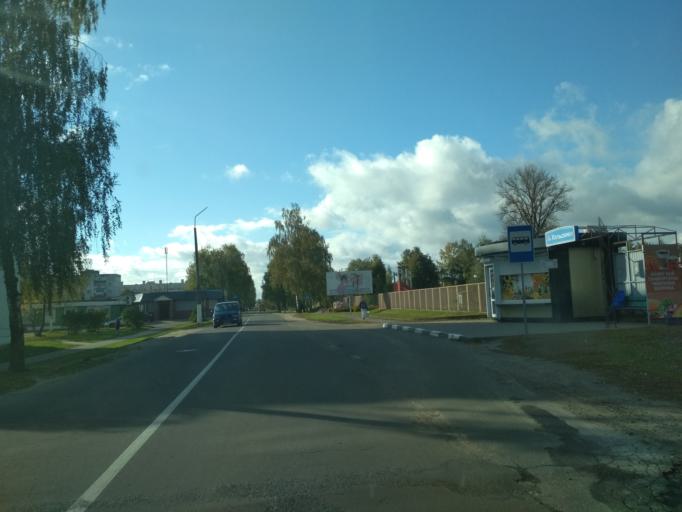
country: BY
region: Minsk
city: Mar''ina Horka
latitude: 53.5049
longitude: 28.1683
